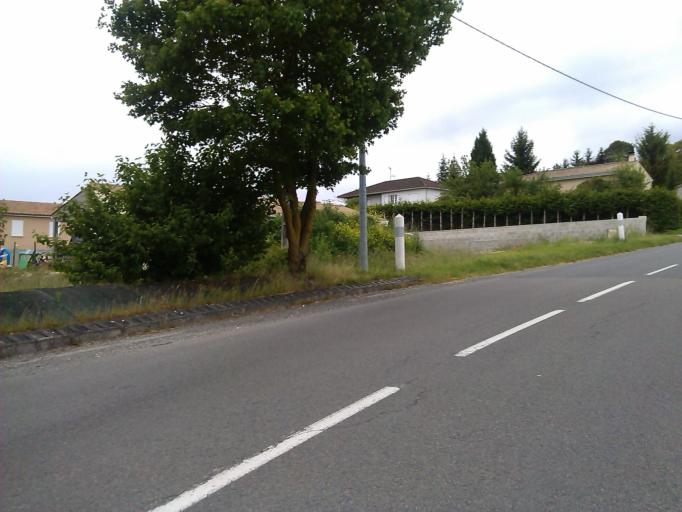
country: FR
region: Poitou-Charentes
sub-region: Departement de la Charente
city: Chateauneuf-sur-Charente
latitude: 45.5899
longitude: -0.0517
